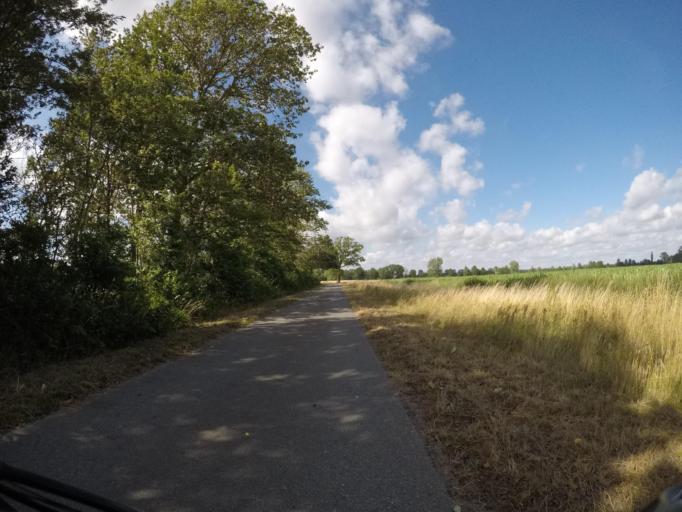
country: DE
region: Lower Saxony
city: Damnatz
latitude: 53.1799
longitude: 11.1697
